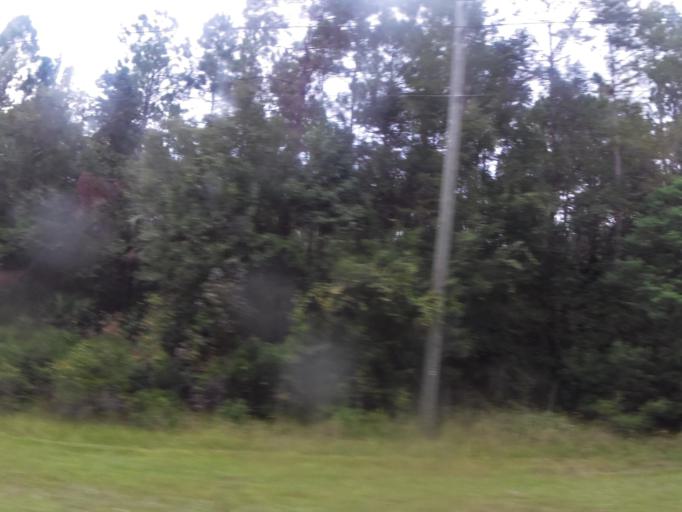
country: US
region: Florida
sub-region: Flagler County
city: Bunnell
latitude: 29.5036
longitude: -81.3423
